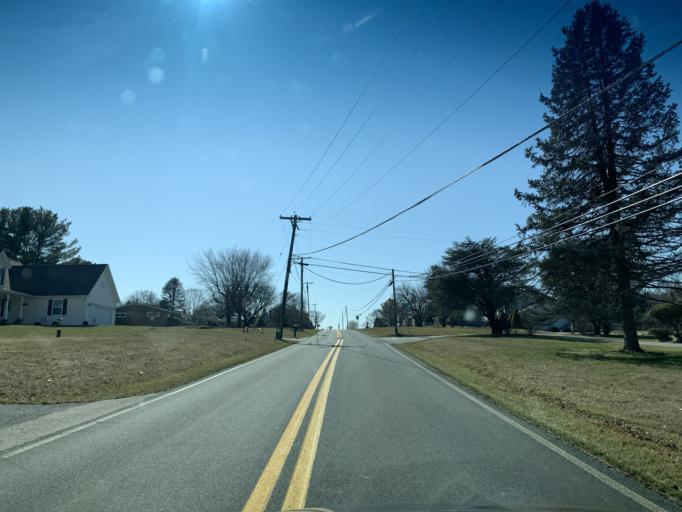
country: US
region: Maryland
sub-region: Carroll County
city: Hampstead
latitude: 39.5875
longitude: -76.8641
